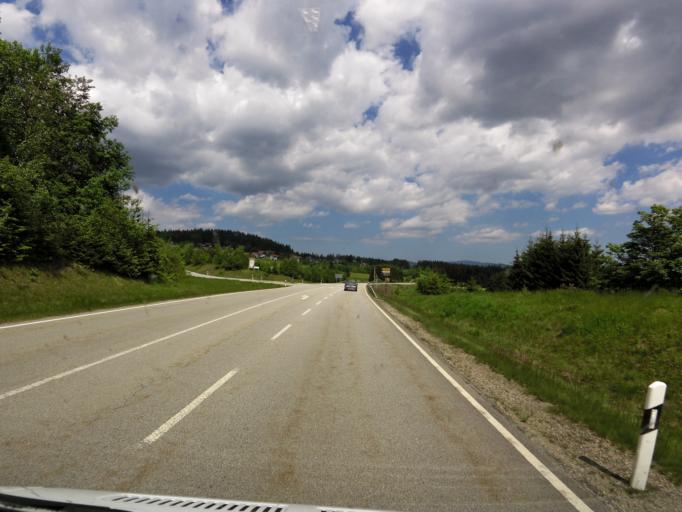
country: DE
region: Bavaria
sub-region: Lower Bavaria
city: Philippsreut
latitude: 48.8613
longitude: 13.6787
